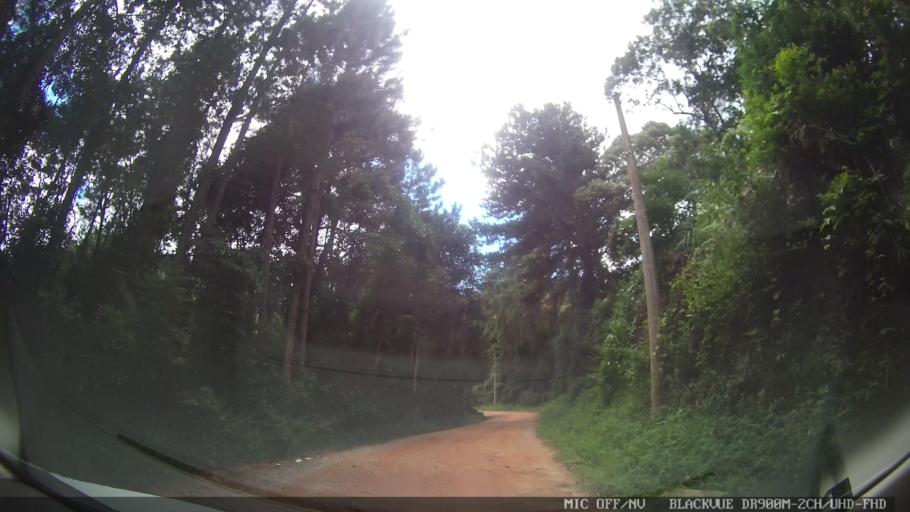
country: BR
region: Minas Gerais
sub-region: Extrema
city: Extrema
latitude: -22.8798
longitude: -46.3195
